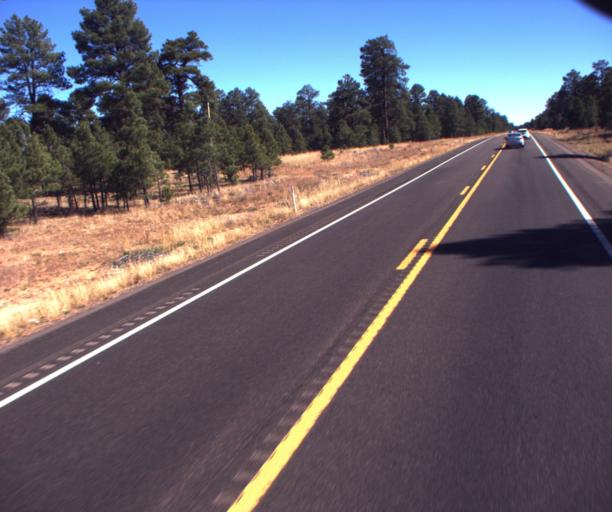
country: US
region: Arizona
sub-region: Apache County
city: Saint Michaels
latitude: 35.6911
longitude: -109.2578
